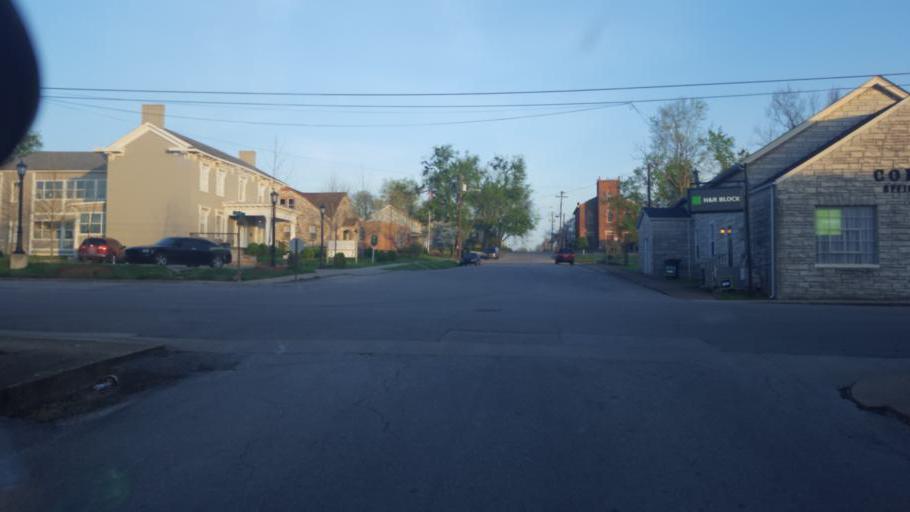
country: US
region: Kentucky
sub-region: Hart County
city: Munfordville
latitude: 37.2704
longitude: -85.8905
